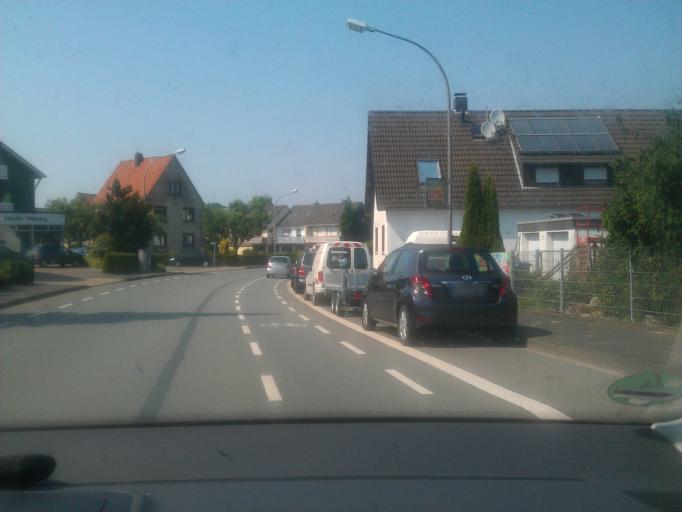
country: DE
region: North Rhine-Westphalia
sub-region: Regierungsbezirk Detmold
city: Oerlinghausen
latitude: 51.9798
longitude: 8.6702
